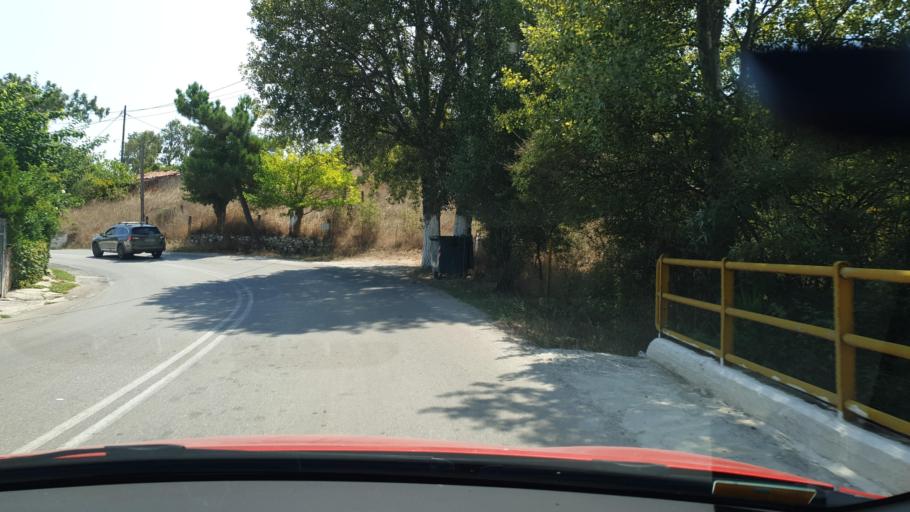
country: GR
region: Central Greece
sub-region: Nomos Evvoias
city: Aliveri
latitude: 38.4653
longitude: 24.1168
